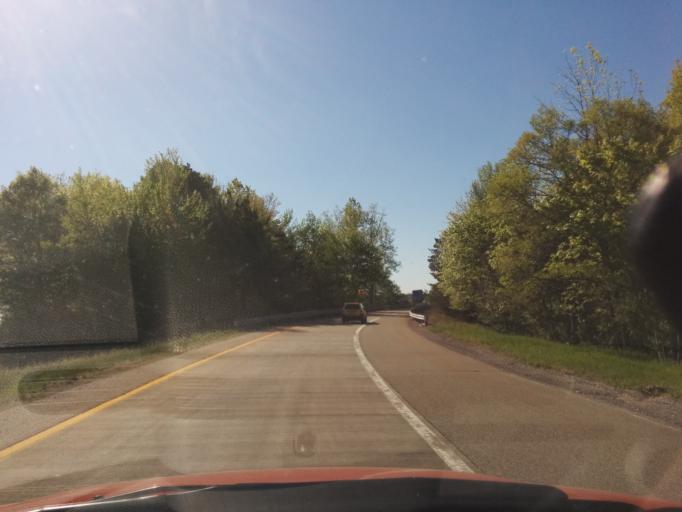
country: US
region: Michigan
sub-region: Midland County
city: Midland
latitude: 43.6562
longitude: -84.2438
